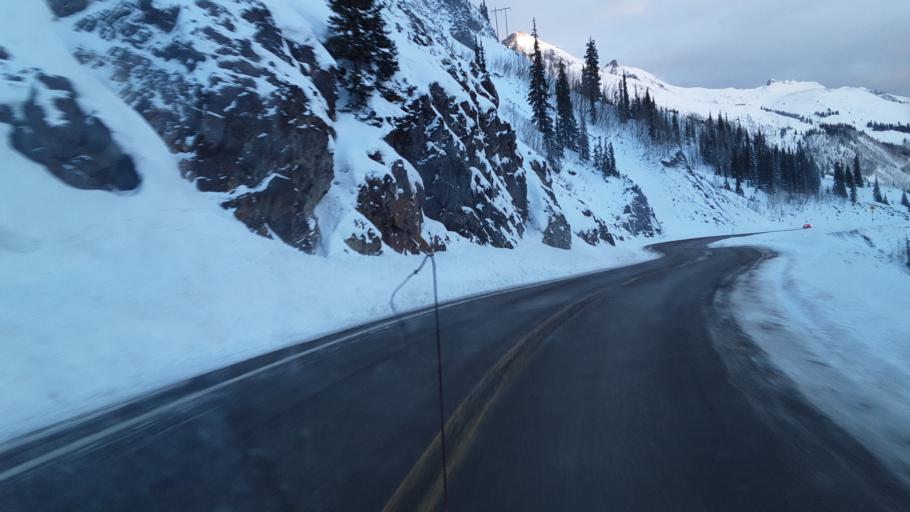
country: US
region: Colorado
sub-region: San Juan County
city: Silverton
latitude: 37.9087
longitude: -107.7061
